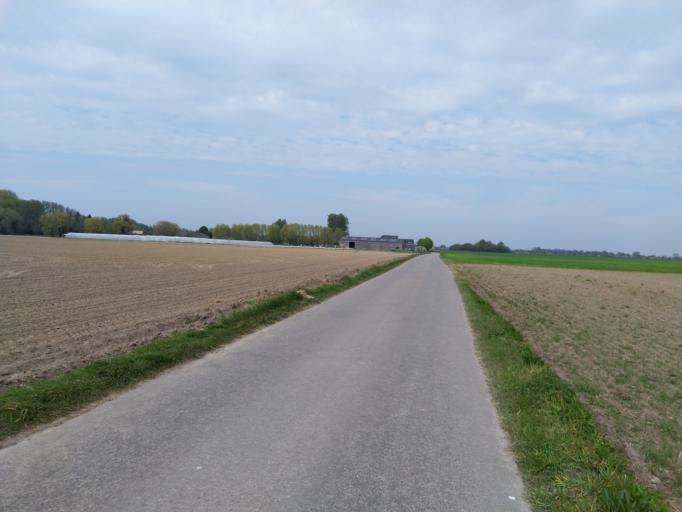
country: BE
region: Wallonia
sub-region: Province du Hainaut
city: Jurbise
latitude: 50.5162
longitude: 3.8838
